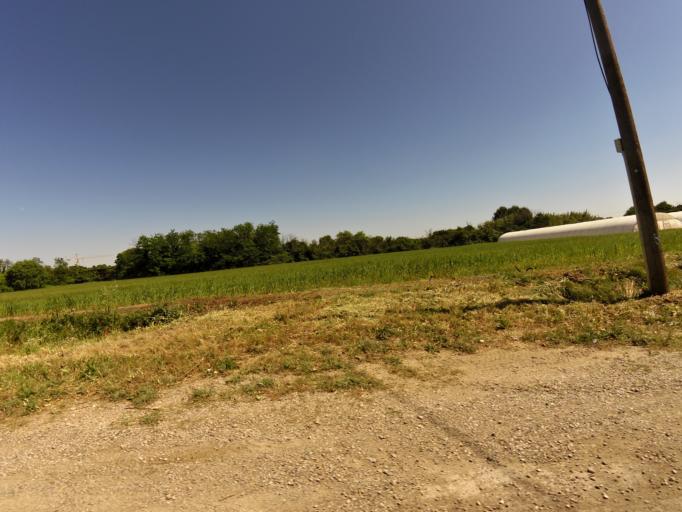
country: FR
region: Languedoc-Roussillon
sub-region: Departement de l'Herault
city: Castries
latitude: 43.6707
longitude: 3.9780
